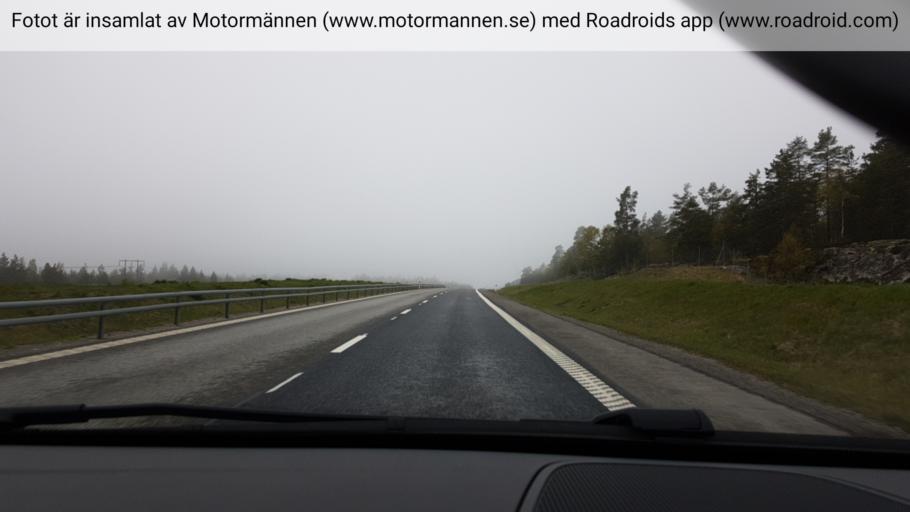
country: SE
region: Stockholm
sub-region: Nynashamns Kommun
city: Osmo
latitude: 59.0502
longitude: 17.9936
